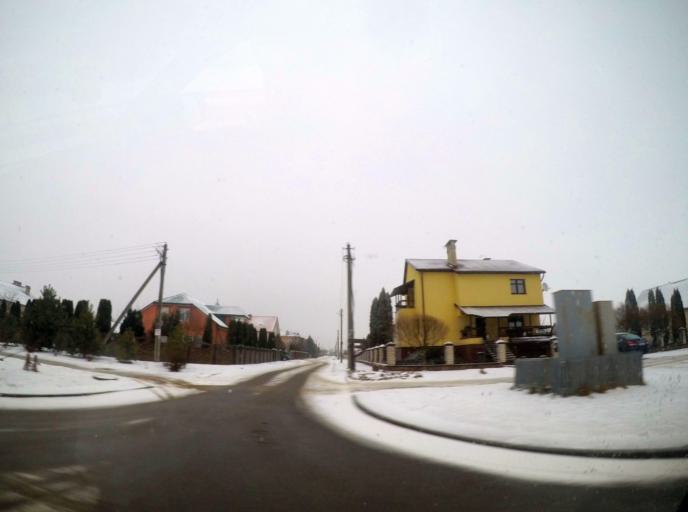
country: BY
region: Grodnenskaya
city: Hrodna
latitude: 53.6261
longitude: 23.8069
